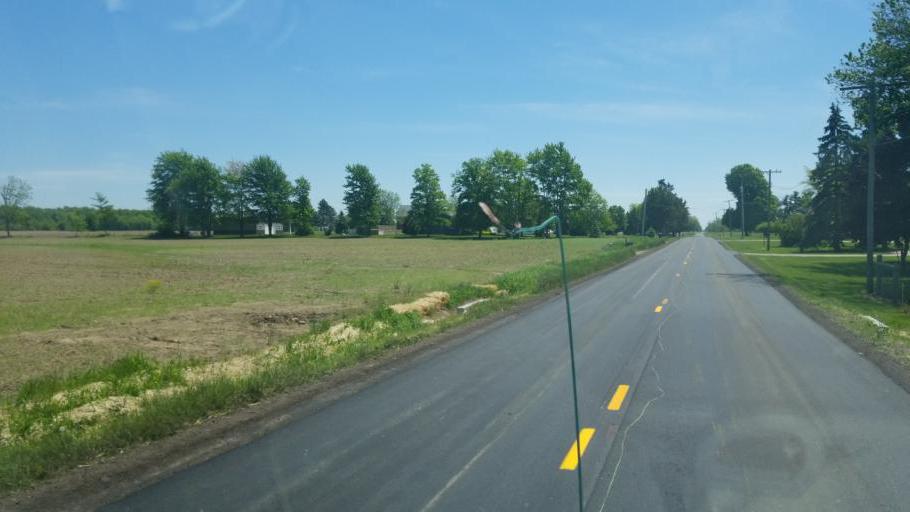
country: US
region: Ohio
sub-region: Huron County
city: Norwalk
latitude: 41.2028
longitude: -82.5902
